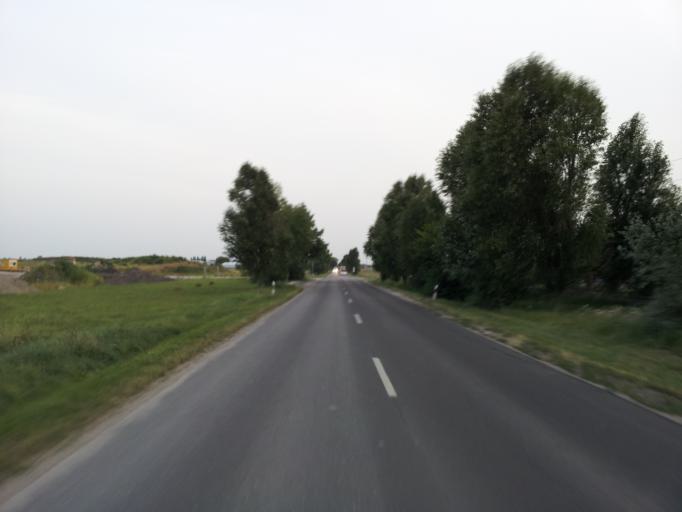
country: HU
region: Pest
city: Szigetszentmiklos
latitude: 47.3683
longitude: 19.0483
